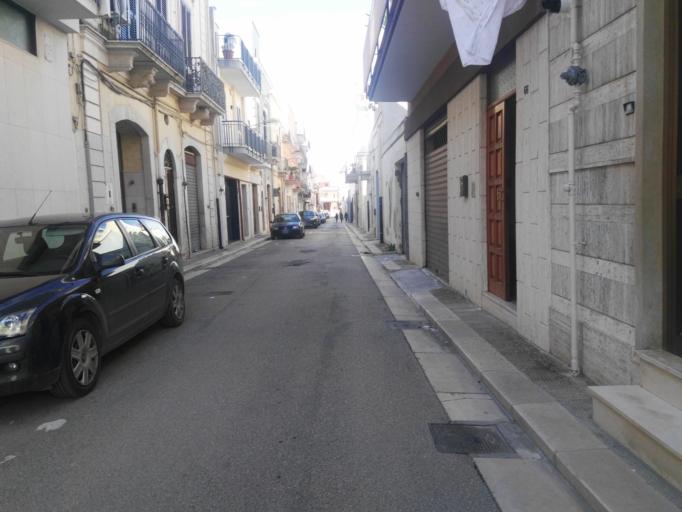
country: IT
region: Apulia
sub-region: Provincia di Barletta - Andria - Trani
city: Andria
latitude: 41.2217
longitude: 16.3014
